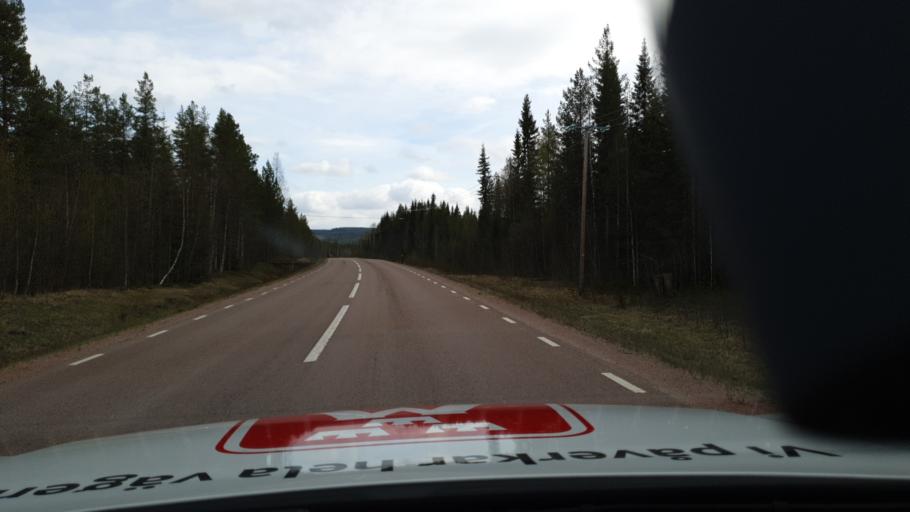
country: SE
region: Jaemtland
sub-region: Braecke Kommun
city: Braecke
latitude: 62.9246
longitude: 15.6790
